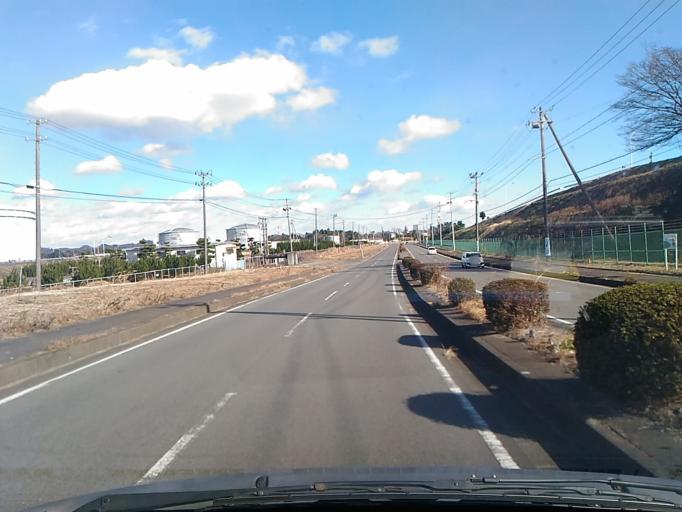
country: JP
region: Fukushima
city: Iwaki
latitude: 36.9284
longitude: 140.8547
